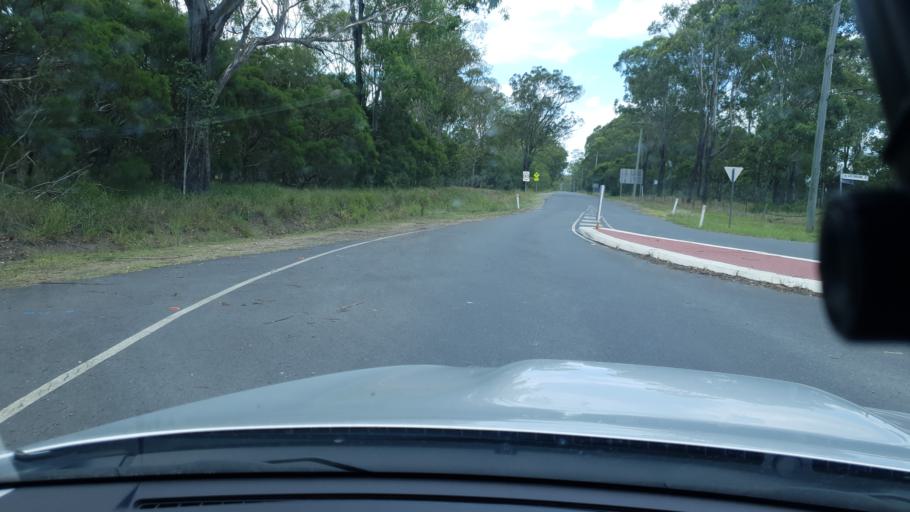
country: AU
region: Queensland
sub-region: Logan
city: North Maclean
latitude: -27.7746
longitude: 153.0085
